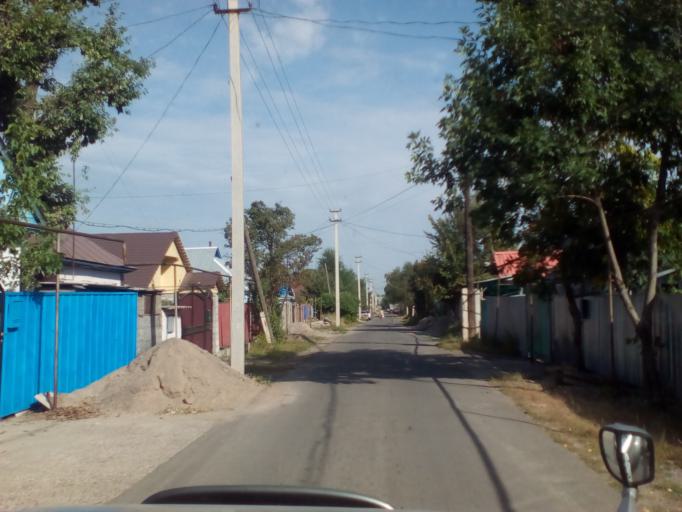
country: KZ
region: Almaty Oblysy
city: Burunday
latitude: 43.1596
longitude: 76.4089
